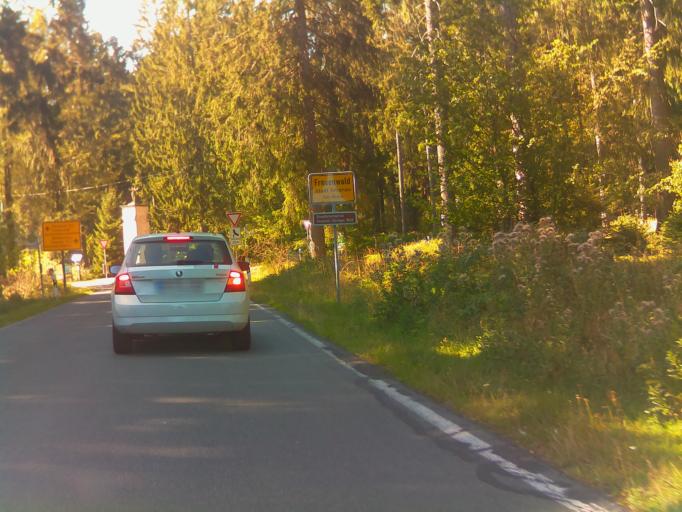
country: DE
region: Thuringia
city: Frauenwald
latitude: 50.5954
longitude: 10.8586
